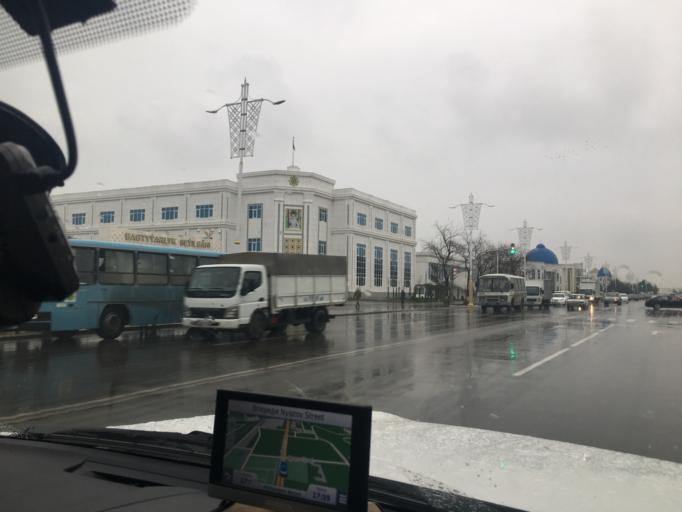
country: TM
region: Mary
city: Mary
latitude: 37.5932
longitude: 61.8405
